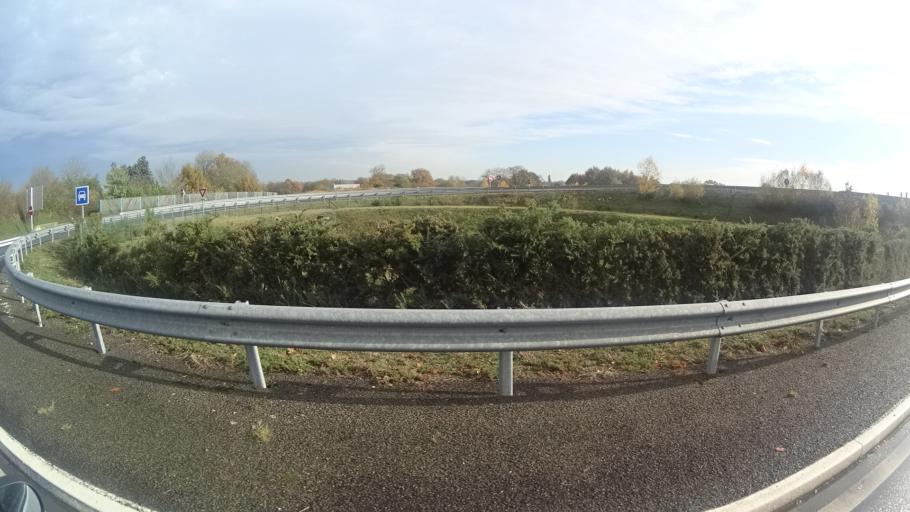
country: FR
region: Brittany
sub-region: Departement du Morbihan
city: Saint-Jean-la-Poterie
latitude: 47.6192
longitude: -2.1148
